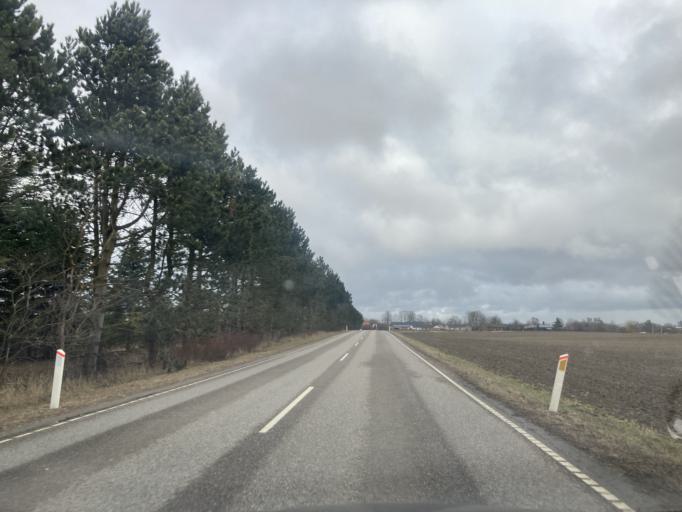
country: DK
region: Zealand
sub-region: Greve Kommune
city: Tune
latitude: 55.6110
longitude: 12.1839
